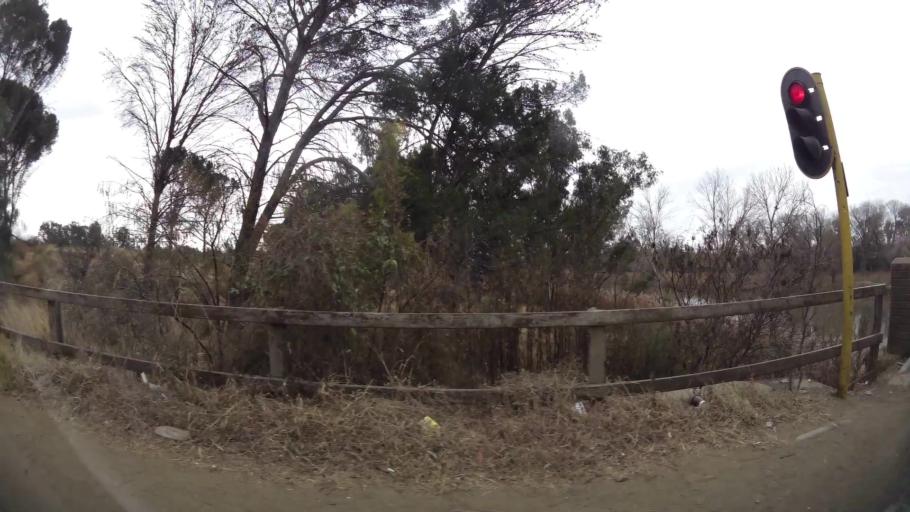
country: ZA
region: Orange Free State
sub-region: Fezile Dabi District Municipality
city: Kroonstad
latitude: -27.6708
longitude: 27.2313
